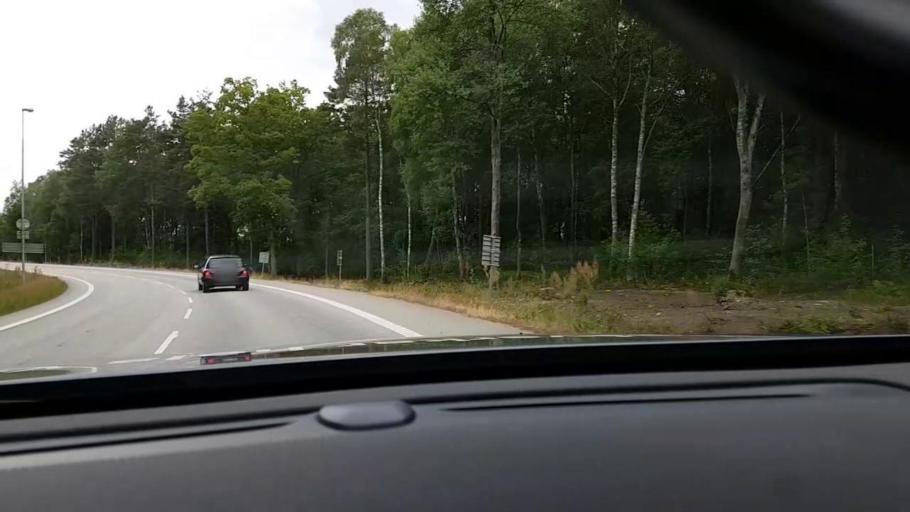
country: SE
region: Skane
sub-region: Hassleholms Kommun
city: Hassleholm
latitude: 56.1723
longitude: 13.7767
